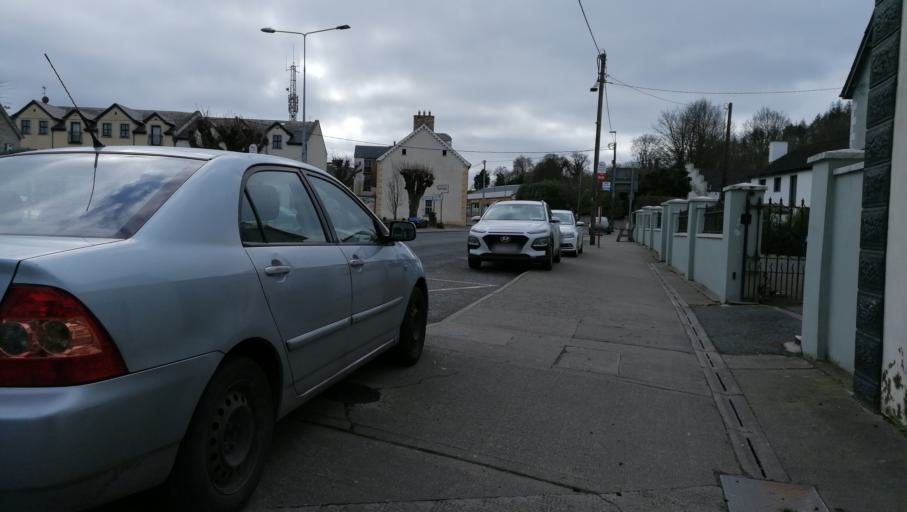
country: IE
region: Ulster
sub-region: County Monaghan
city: Castleblayney
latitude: 54.1192
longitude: -6.7368
